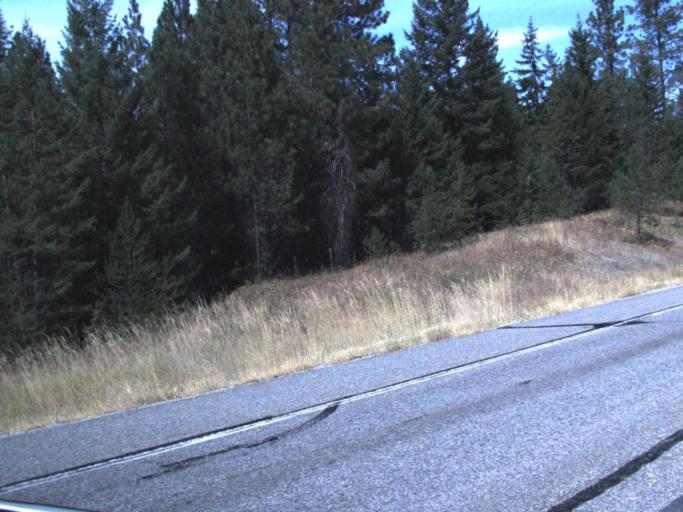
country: US
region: Washington
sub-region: Stevens County
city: Chewelah
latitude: 48.1237
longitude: -117.6505
